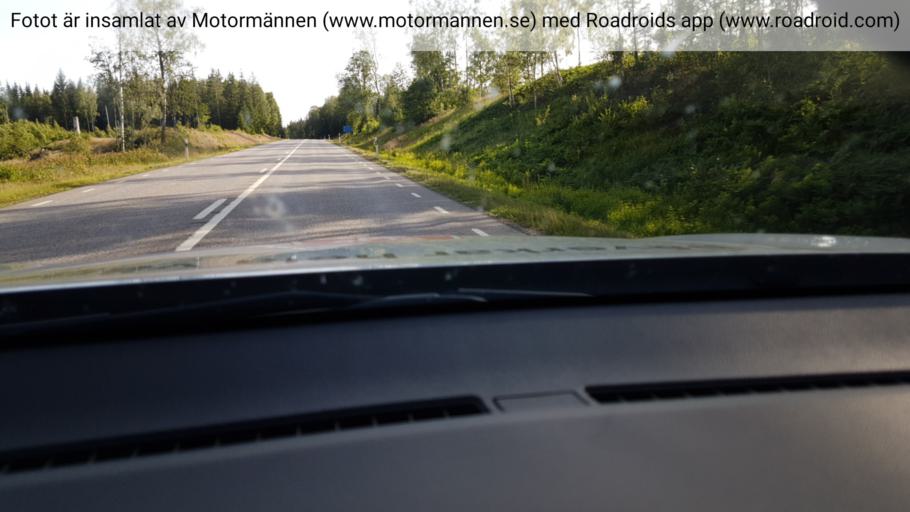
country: SE
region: Joenkoeping
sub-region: Varnamo Kommun
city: Bor
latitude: 57.2585
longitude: 14.1878
